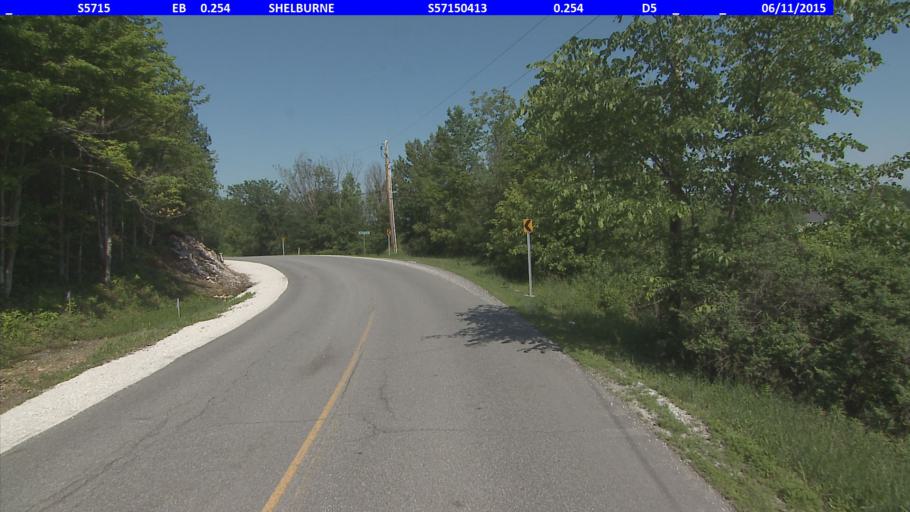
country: US
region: Vermont
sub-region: Chittenden County
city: Hinesburg
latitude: 44.3651
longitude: -73.1655
